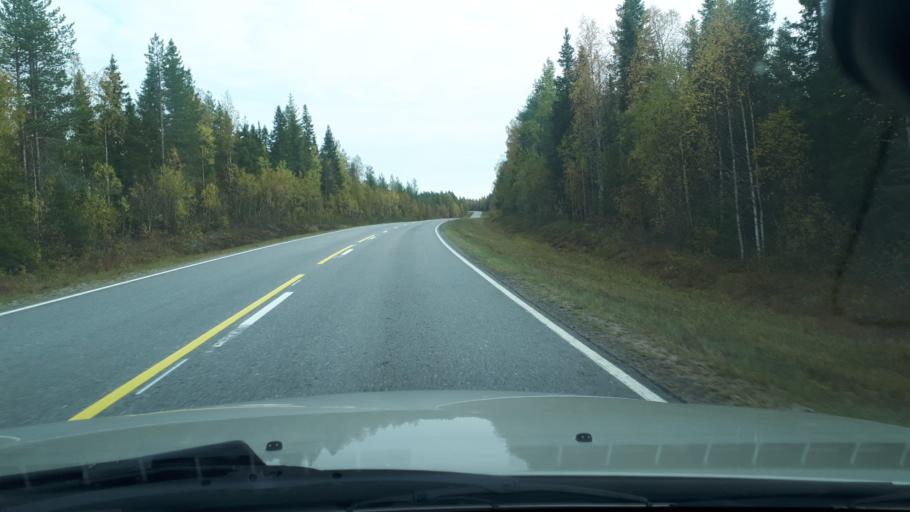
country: FI
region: Lapland
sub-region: Rovaniemi
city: Ranua
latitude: 66.0022
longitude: 26.2480
